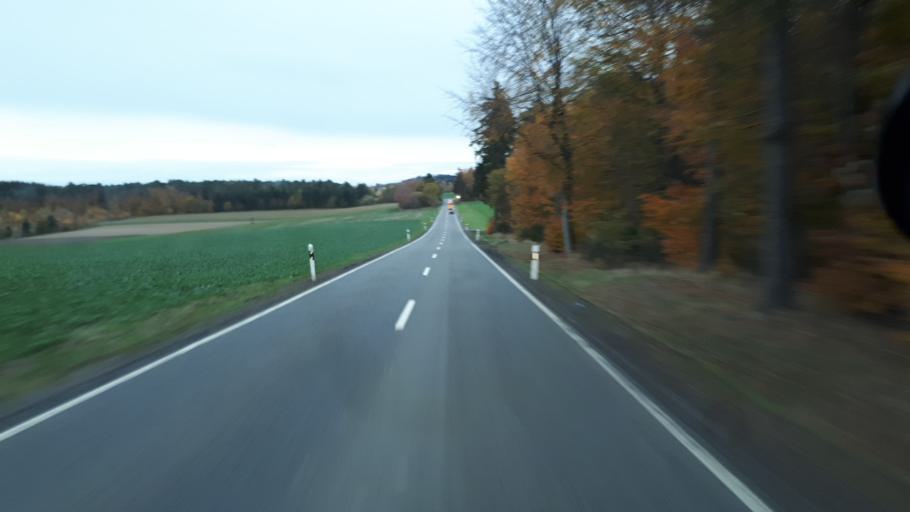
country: DE
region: Rheinland-Pfalz
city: Kaisersesch
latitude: 50.2122
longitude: 7.1312
